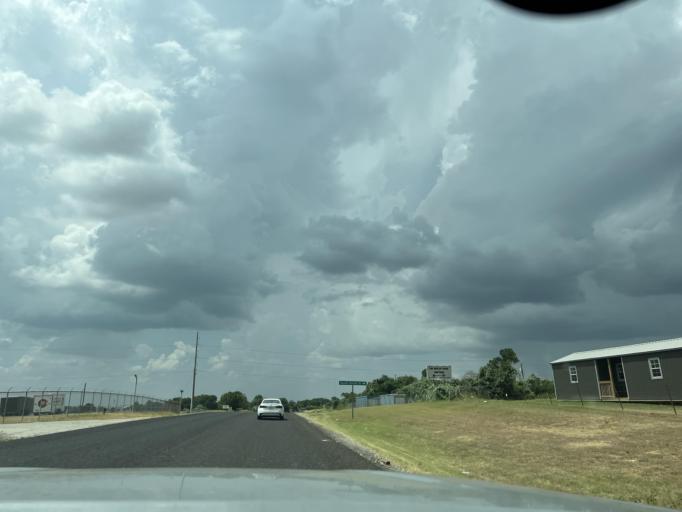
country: US
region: Texas
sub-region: Wise County
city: Decatur
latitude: 33.2012
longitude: -97.6038
